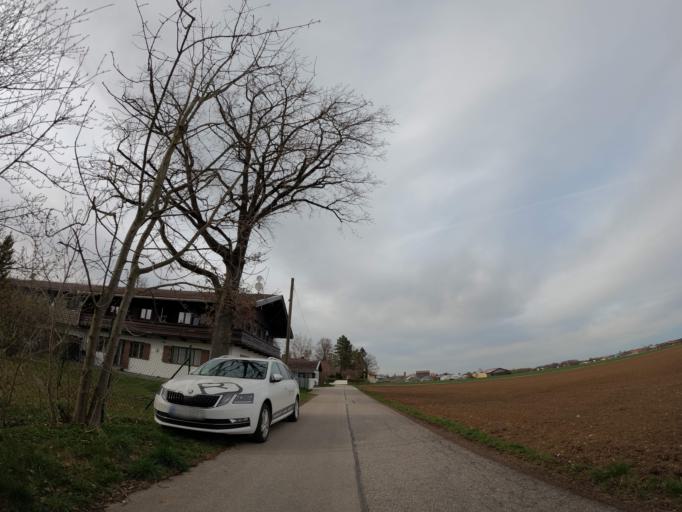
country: DE
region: Bavaria
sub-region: Upper Bavaria
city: Taufkirchen
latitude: 48.0339
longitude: 11.6179
